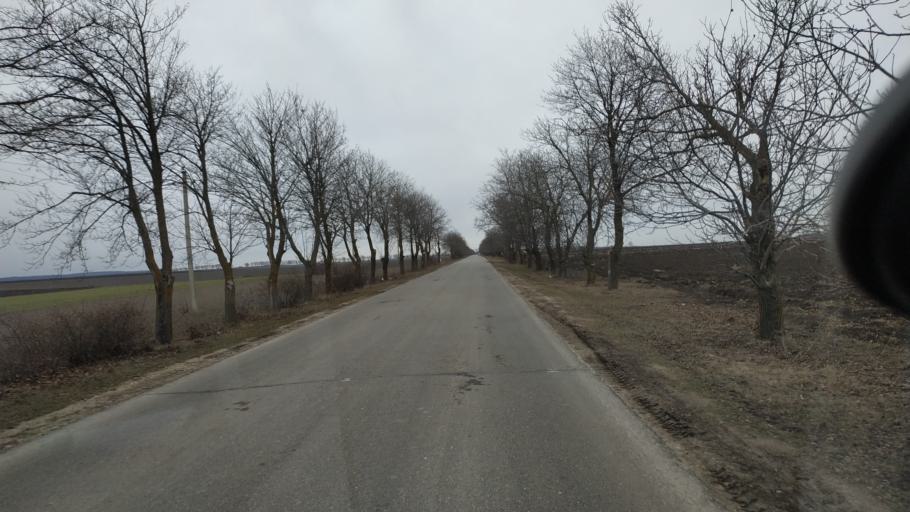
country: MD
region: Telenesti
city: Cocieri
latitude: 47.3121
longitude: 29.0572
